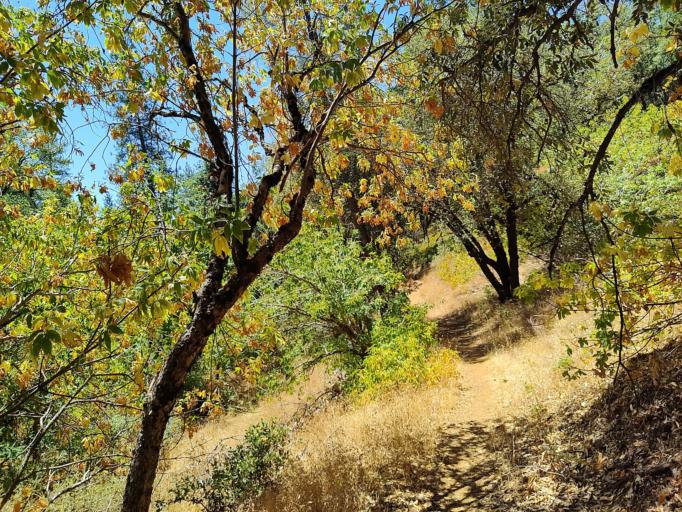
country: US
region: California
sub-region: Placer County
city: Meadow Vista
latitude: 39.0319
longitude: -120.9889
